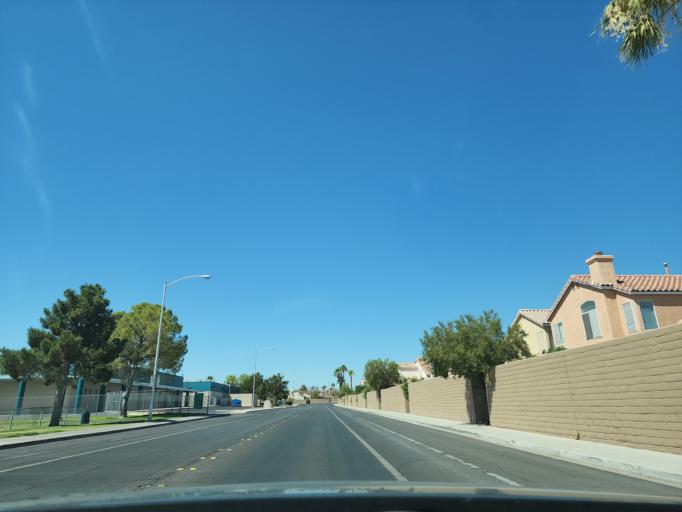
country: US
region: Nevada
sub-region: Clark County
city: Spring Valley
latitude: 36.1073
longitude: -115.2548
